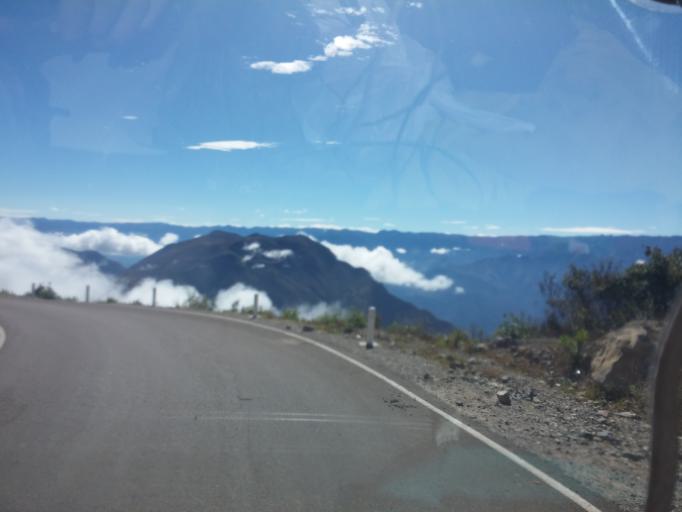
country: PE
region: Cajamarca
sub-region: Provincia de Celendin
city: Celendin
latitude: -6.8705
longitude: -78.1120
